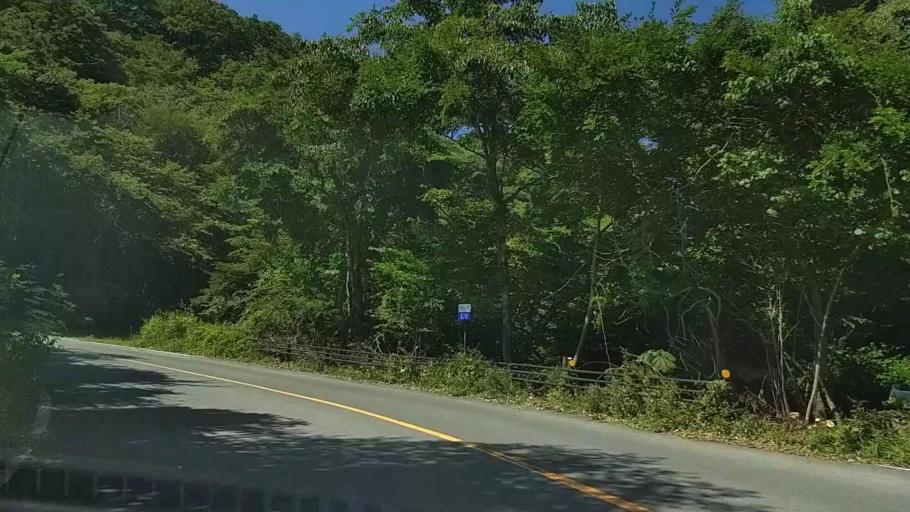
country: JP
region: Nagano
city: Saku
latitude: 36.3546
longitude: 138.6653
